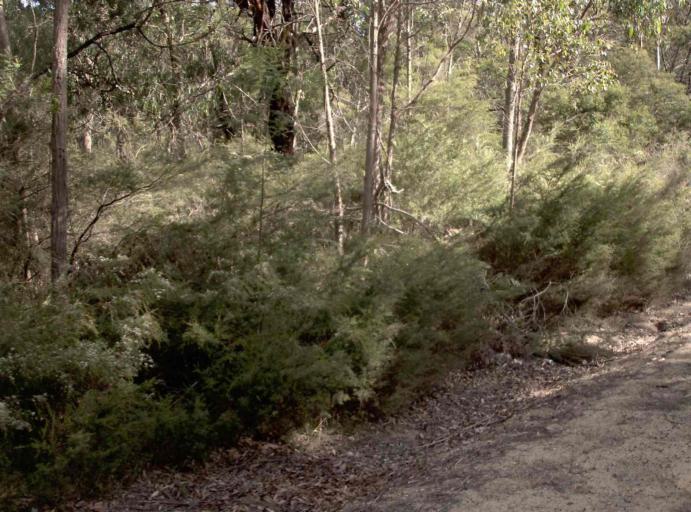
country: AU
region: Victoria
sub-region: East Gippsland
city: Lakes Entrance
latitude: -37.5502
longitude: 148.1478
